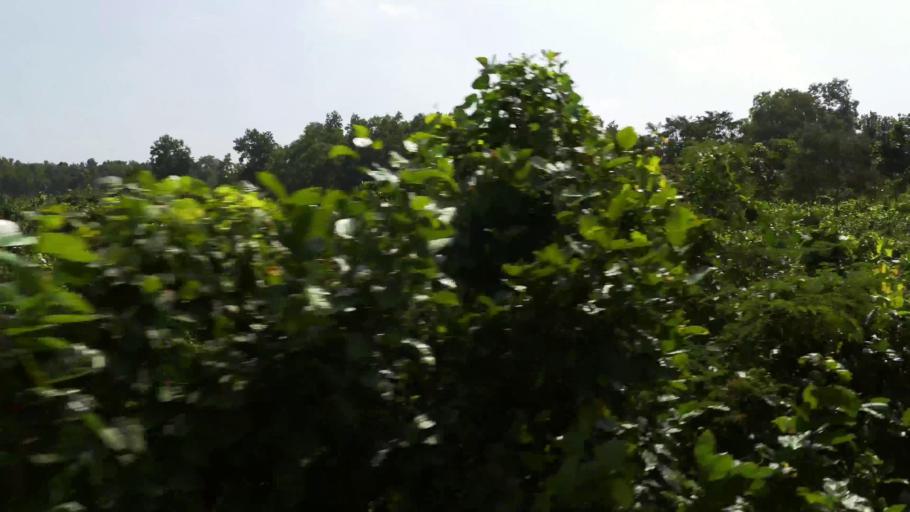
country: BD
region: Dhaka
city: Tungi
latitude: 24.1580
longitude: 90.4672
